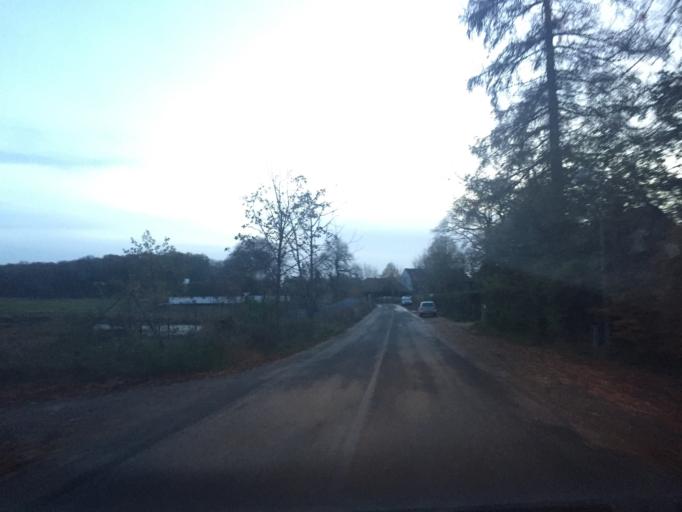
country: DK
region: Capital Region
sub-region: Rudersdal Kommune
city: Trorod
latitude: 55.8008
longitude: 12.5463
